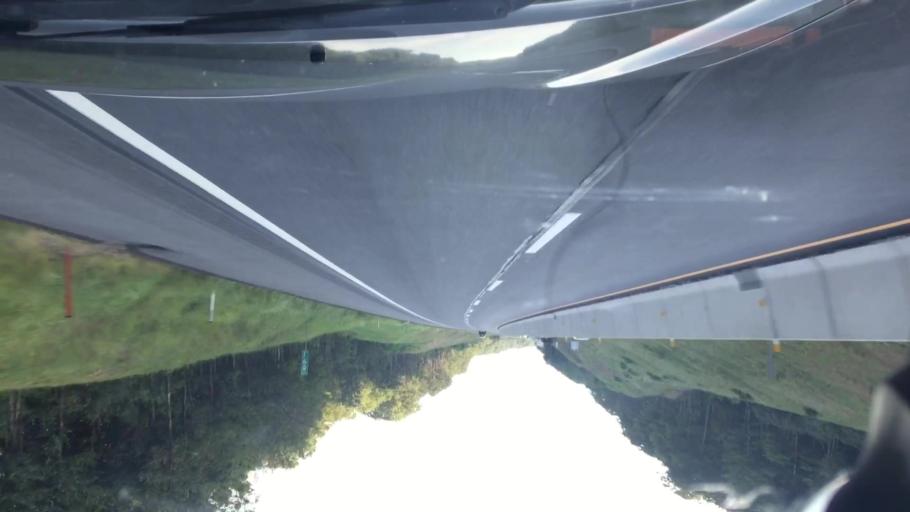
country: US
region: Pennsylvania
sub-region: Carbon County
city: Towamensing Trails
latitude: 41.0118
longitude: -75.6377
